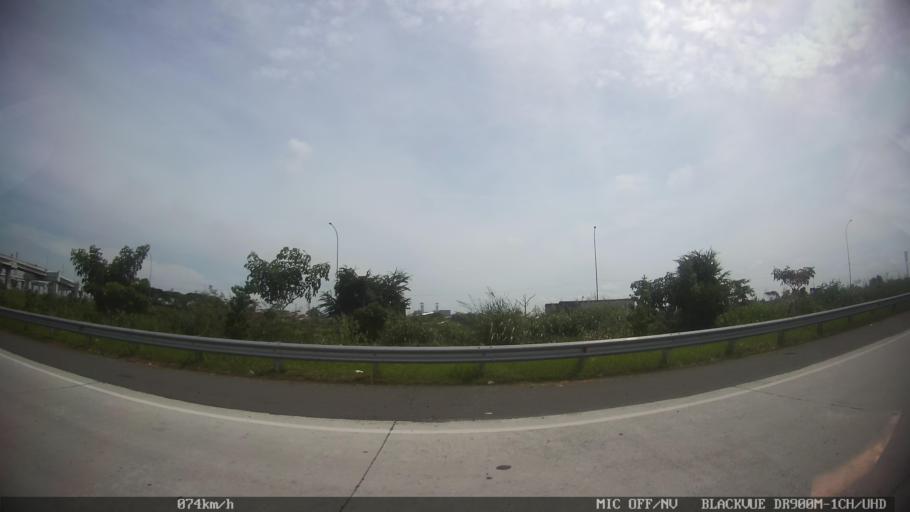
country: ID
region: North Sumatra
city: Medan
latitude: 3.6492
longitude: 98.6830
